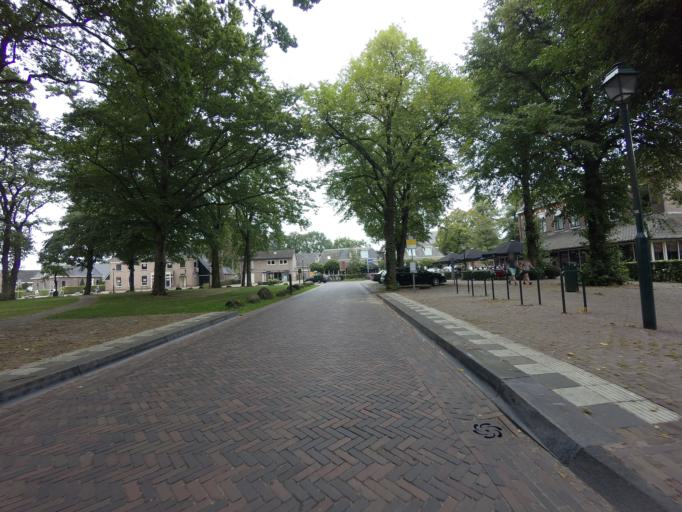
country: NL
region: Drenthe
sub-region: Gemeente Westerveld
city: Dwingeloo
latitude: 52.8339
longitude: 6.3658
